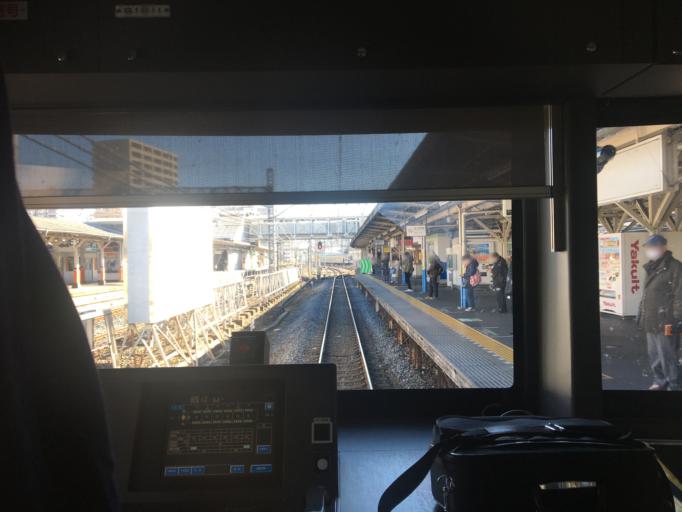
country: JP
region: Saitama
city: Kasukabe
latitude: 35.9802
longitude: 139.7520
